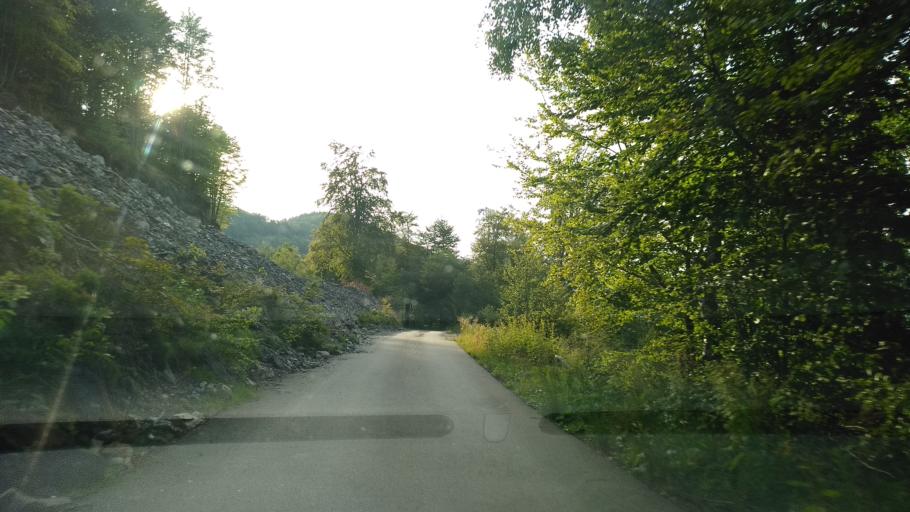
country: RO
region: Hunedoara
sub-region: Municipiul  Vulcan
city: Jiu-Paroseni
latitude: 45.3193
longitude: 23.3010
